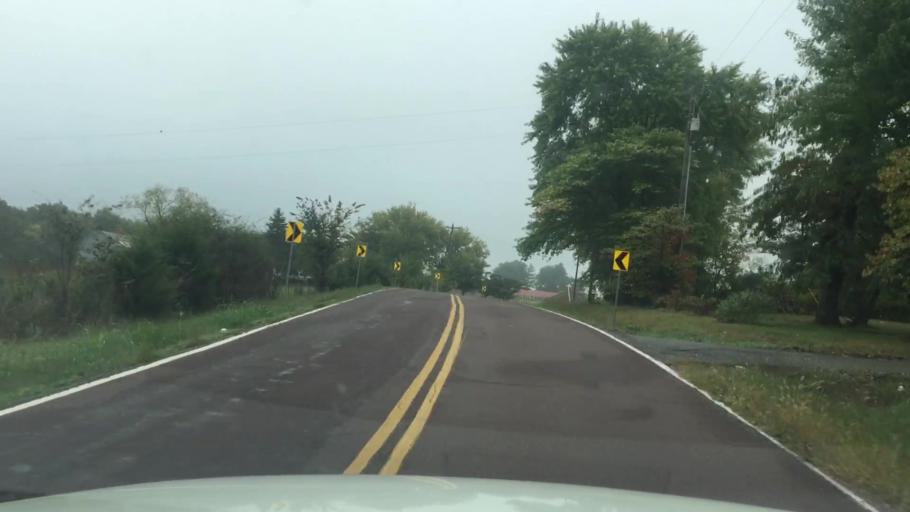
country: US
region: Missouri
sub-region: Boone County
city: Ashland
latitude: 38.8291
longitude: -92.3519
